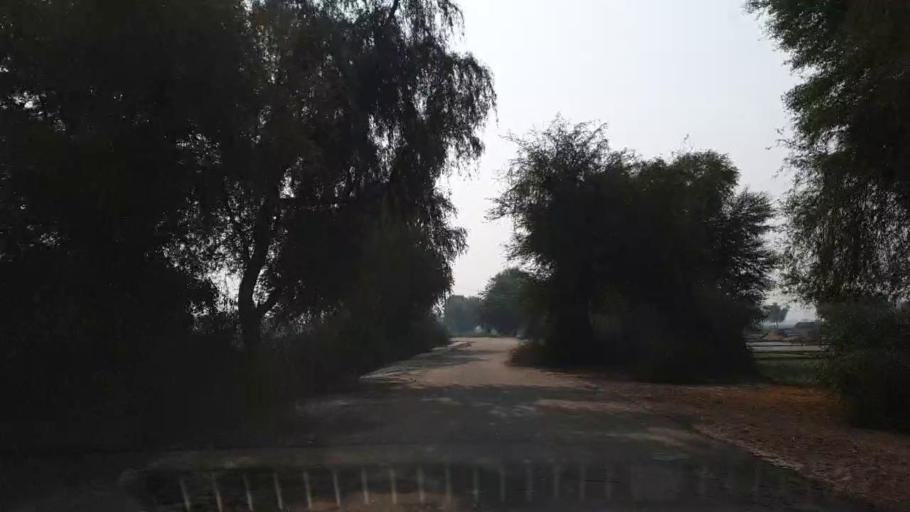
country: PK
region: Sindh
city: Bhan
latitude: 26.5140
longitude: 67.7415
